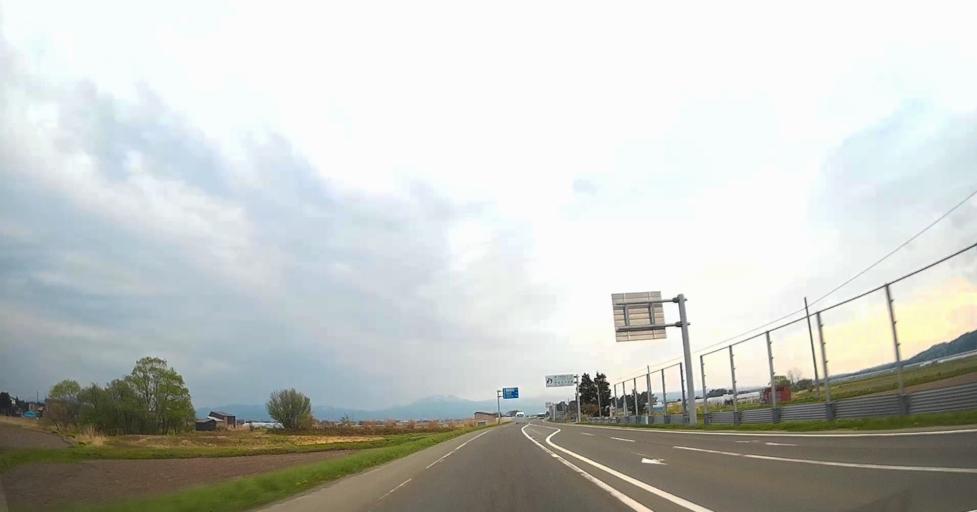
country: JP
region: Aomori
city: Aomori Shi
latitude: 40.9030
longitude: 140.6655
